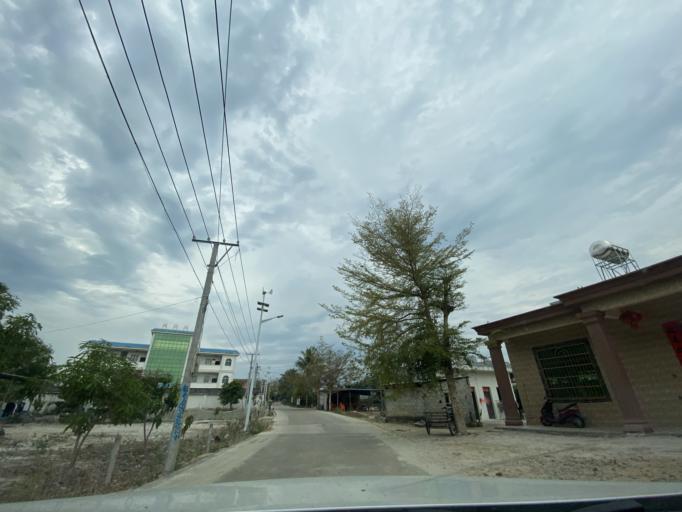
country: CN
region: Hainan
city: Yingzhou
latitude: 18.4149
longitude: 109.8224
